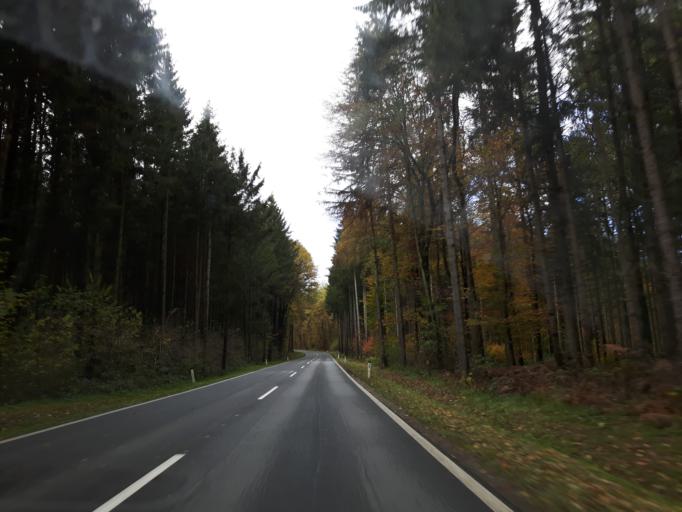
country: AT
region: Styria
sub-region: Politischer Bezirk Leibnitz
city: Breitenfeld am Tannenriegel
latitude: 46.8423
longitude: 15.6275
